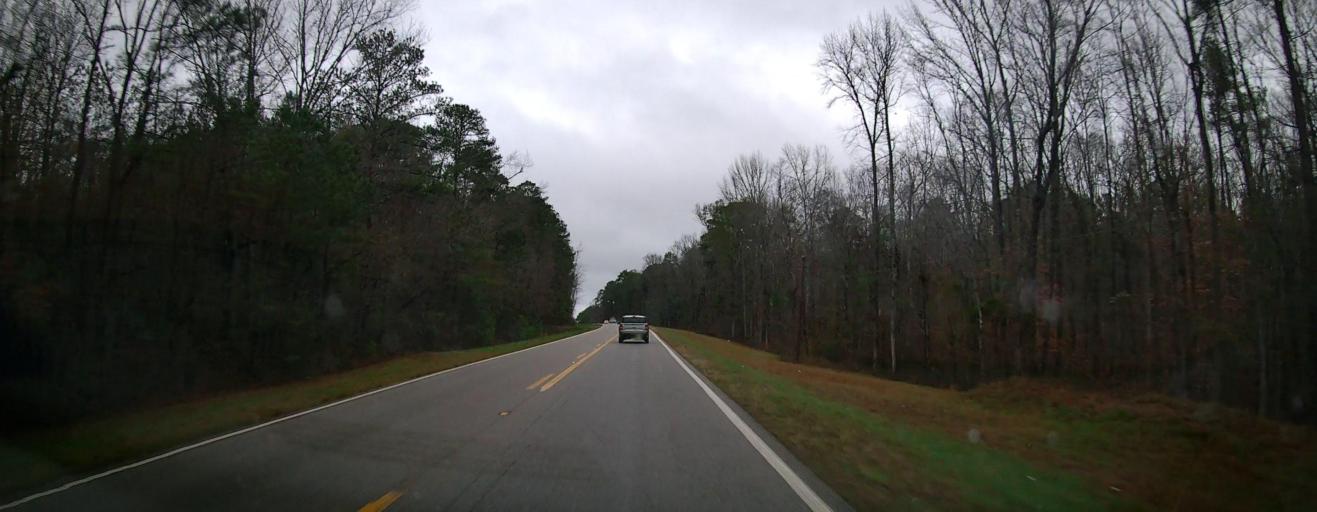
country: US
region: Alabama
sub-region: Bibb County
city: Centreville
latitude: 32.8939
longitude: -86.9886
